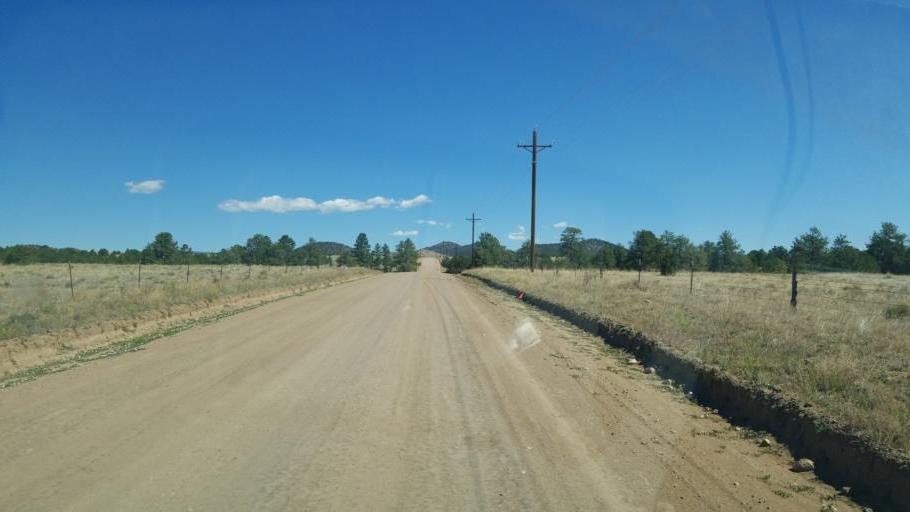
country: US
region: Colorado
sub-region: Custer County
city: Westcliffe
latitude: 38.2739
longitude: -105.5010
